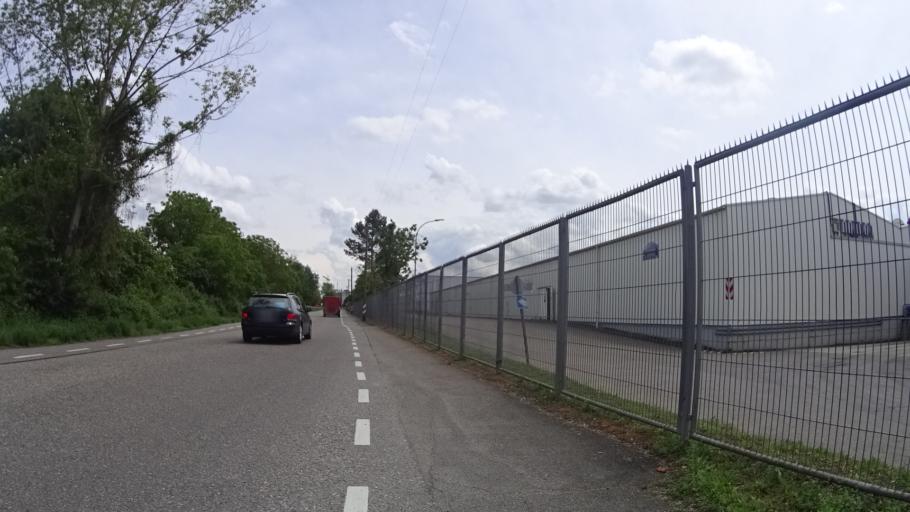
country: CH
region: Basel-City
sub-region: Basel-Stadt
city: Bettingen
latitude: 47.5516
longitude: 7.6538
